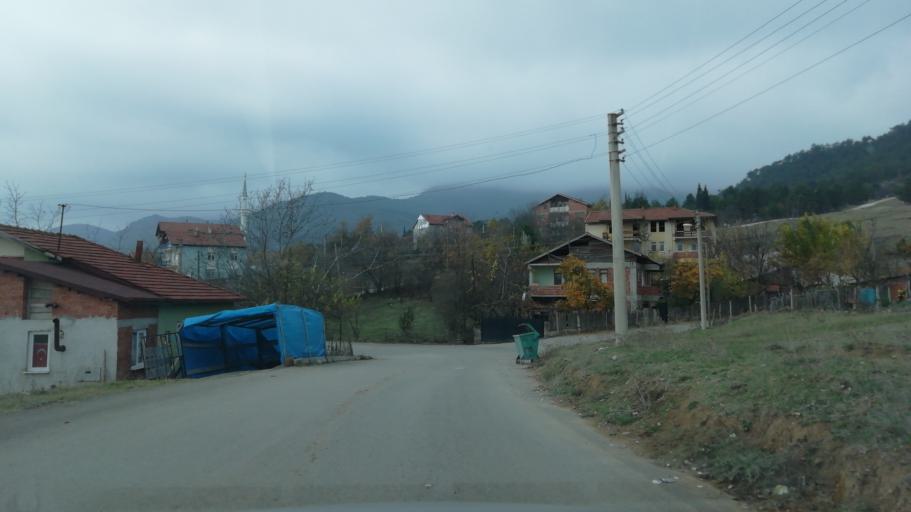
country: TR
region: Karabuk
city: Karabuk
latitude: 41.2317
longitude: 32.6276
